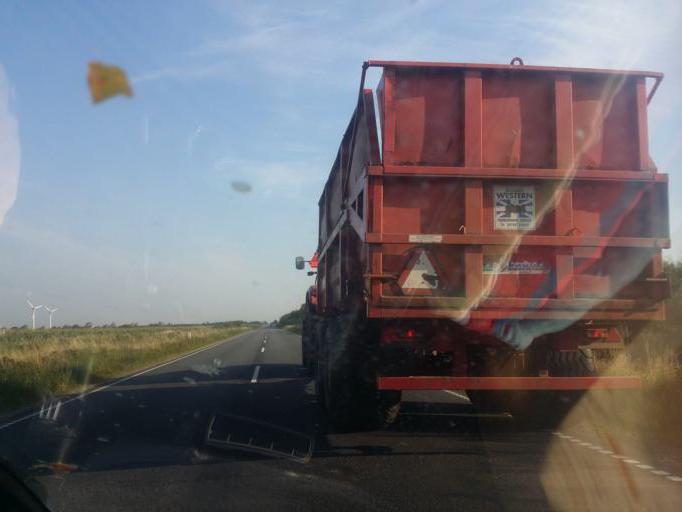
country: DK
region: South Denmark
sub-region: Tonder Kommune
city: Sherrebek
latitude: 55.2018
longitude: 8.7265
